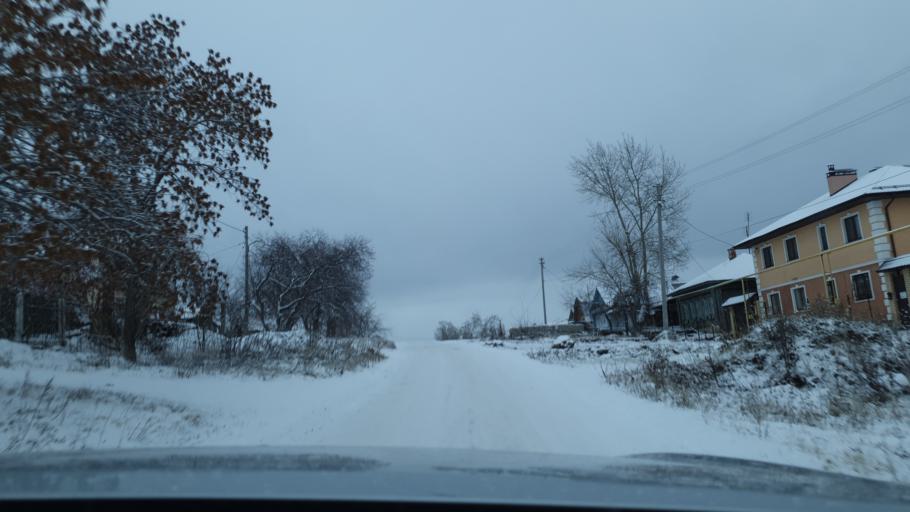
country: RU
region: Sverdlovsk
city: Istok
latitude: 56.7451
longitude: 60.6971
